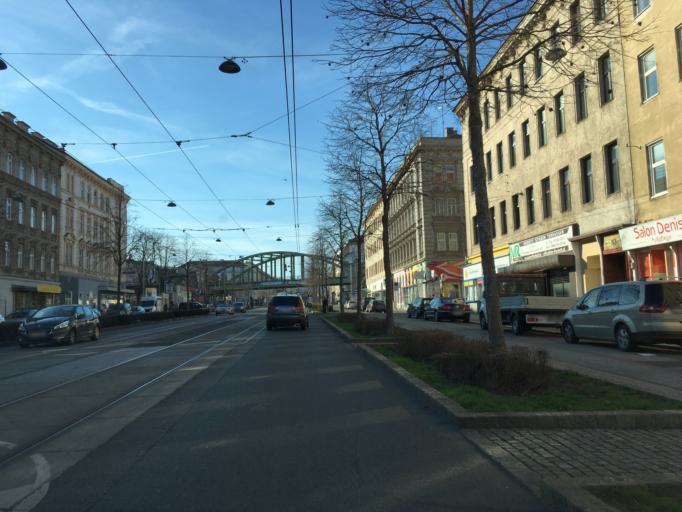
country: AT
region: Vienna
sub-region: Wien Stadt
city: Vienna
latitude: 48.2229
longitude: 16.3177
